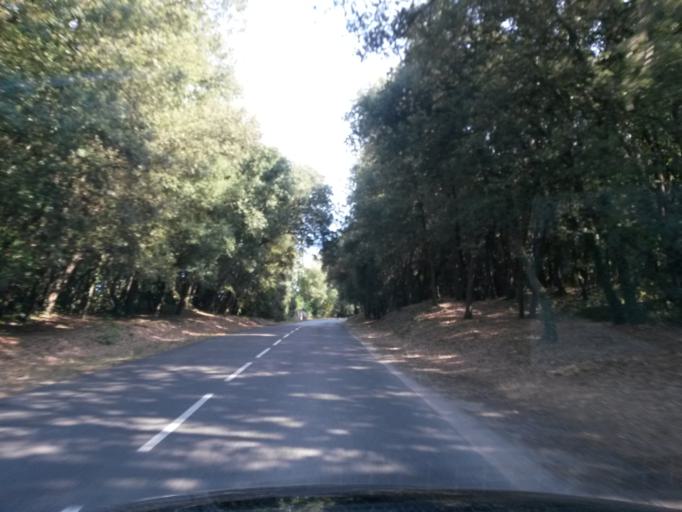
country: FR
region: Pays de la Loire
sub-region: Departement de la Vendee
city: Olonne-sur-Mer
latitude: 46.5291
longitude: -1.8116
